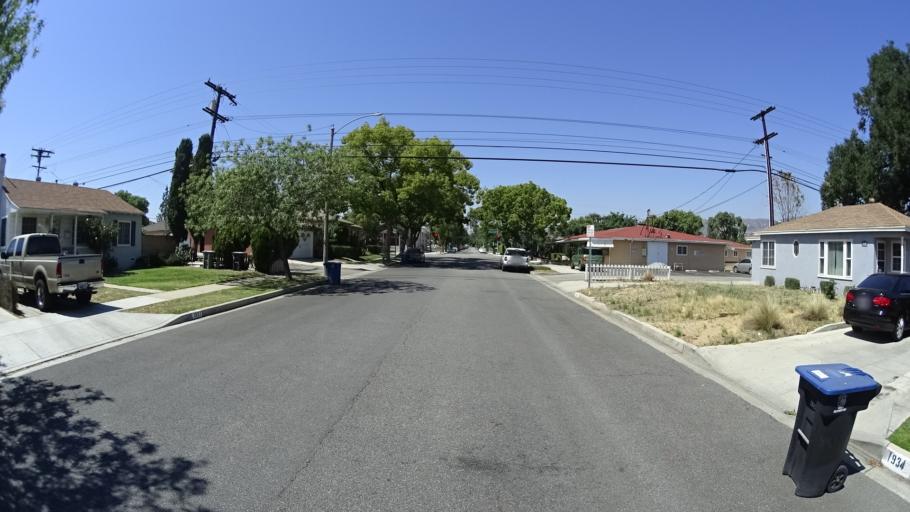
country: US
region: California
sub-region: Los Angeles County
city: North Hollywood
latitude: 34.1841
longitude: -118.3536
